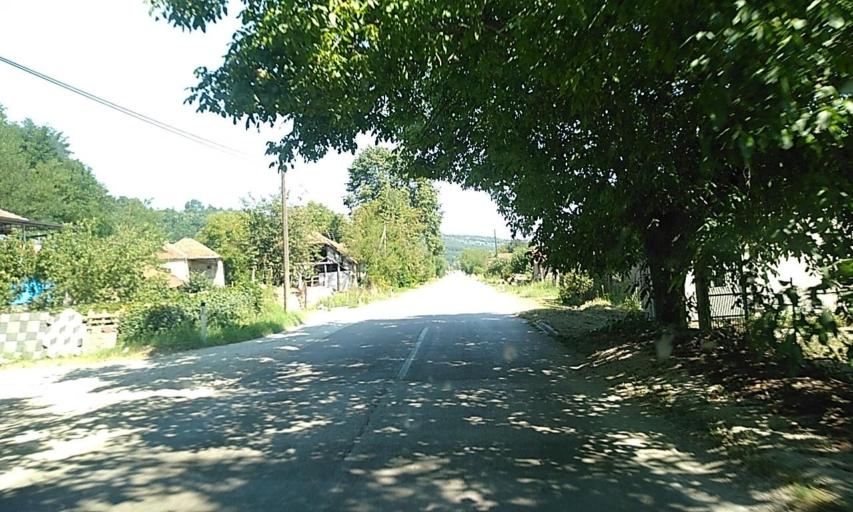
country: RS
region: Central Serbia
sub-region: Pcinjski Okrug
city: Vladicin Han
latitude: 42.6629
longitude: 22.0460
